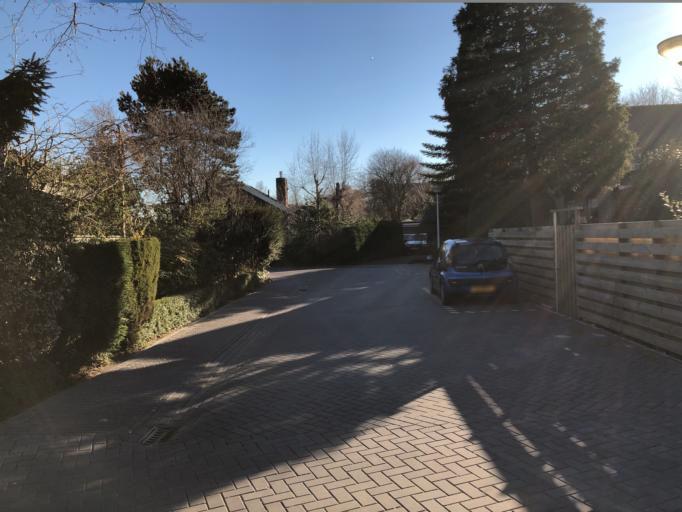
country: NL
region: North Holland
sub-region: Gemeente Uitgeest
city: Uitgeest
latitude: 52.5044
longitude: 4.7552
